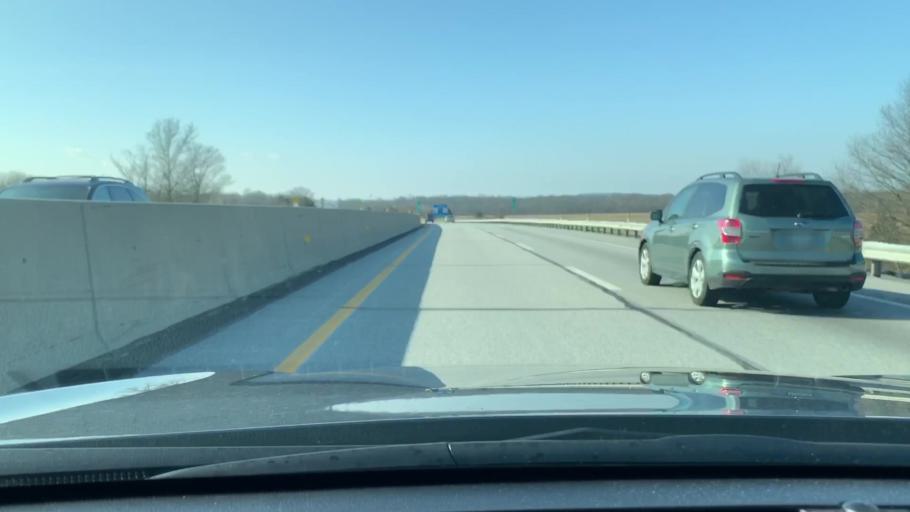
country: US
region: Pennsylvania
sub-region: Lebanon County
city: Campbelltown
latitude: 40.2102
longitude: -76.5506
